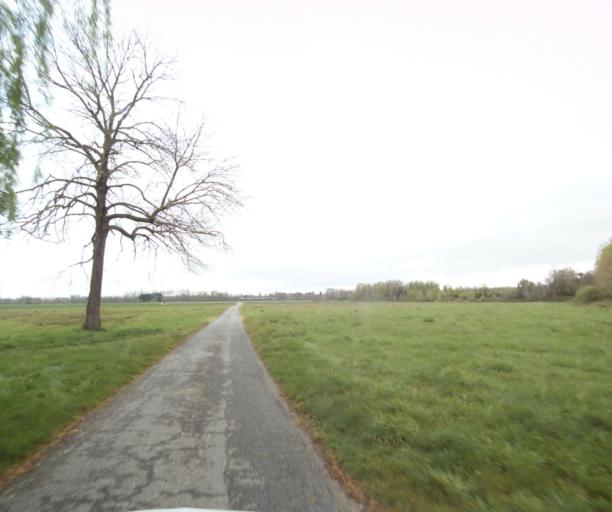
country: FR
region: Midi-Pyrenees
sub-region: Departement de l'Ariege
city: Saverdun
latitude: 43.2189
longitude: 1.5995
